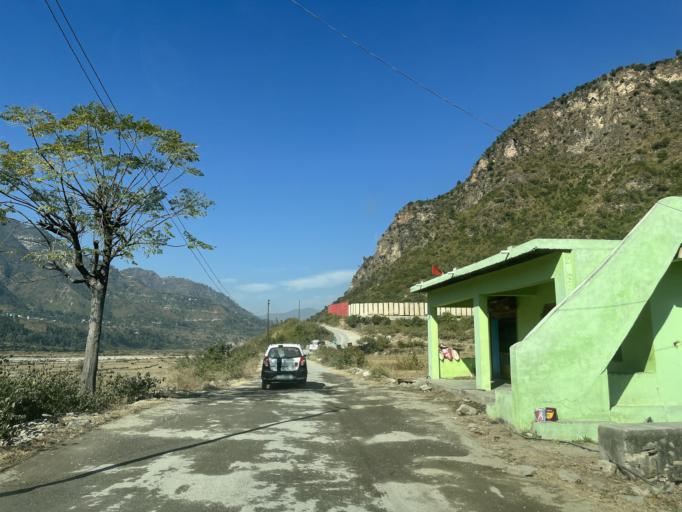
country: IN
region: Uttarakhand
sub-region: Naini Tal
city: Naini Tal
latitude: 29.5084
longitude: 79.4444
